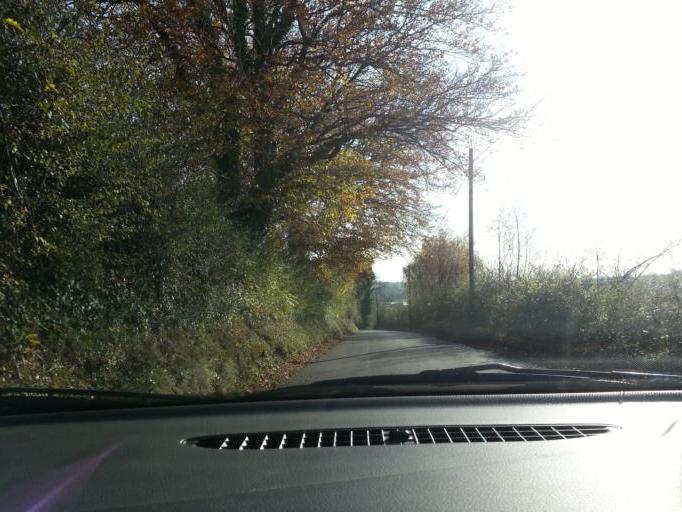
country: GB
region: Northern Ireland
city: Lisnaskea
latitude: 54.2286
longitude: -7.3525
